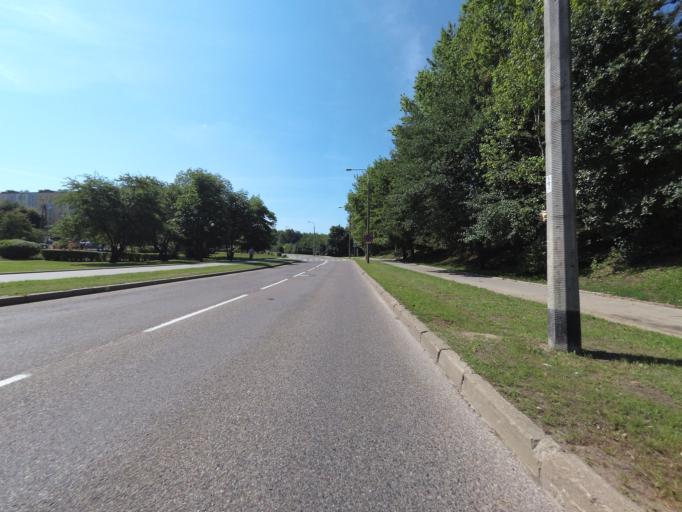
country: PL
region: Pomeranian Voivodeship
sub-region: Gdynia
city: Wielki Kack
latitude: 54.4943
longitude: 18.5078
